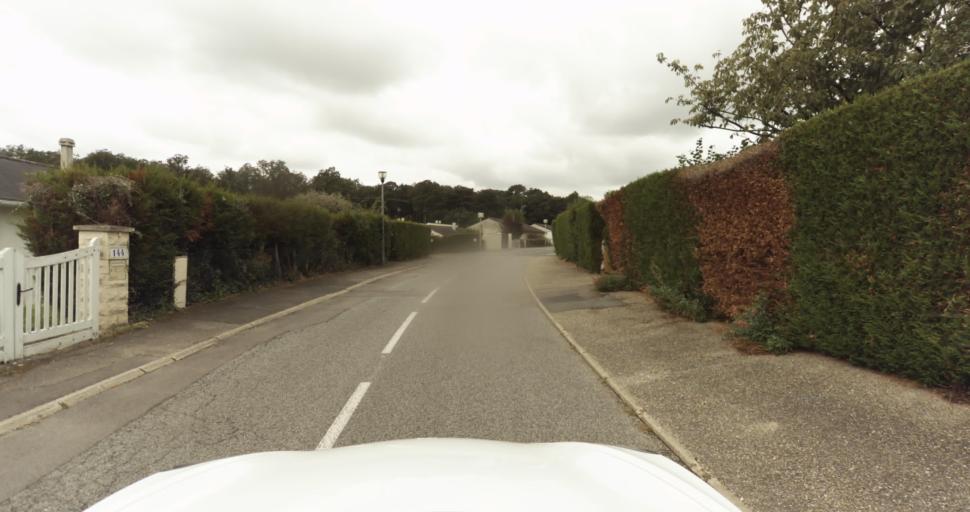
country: FR
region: Haute-Normandie
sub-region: Departement de l'Eure
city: Saint-Sebastien-de-Morsent
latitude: 49.0058
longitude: 1.0948
